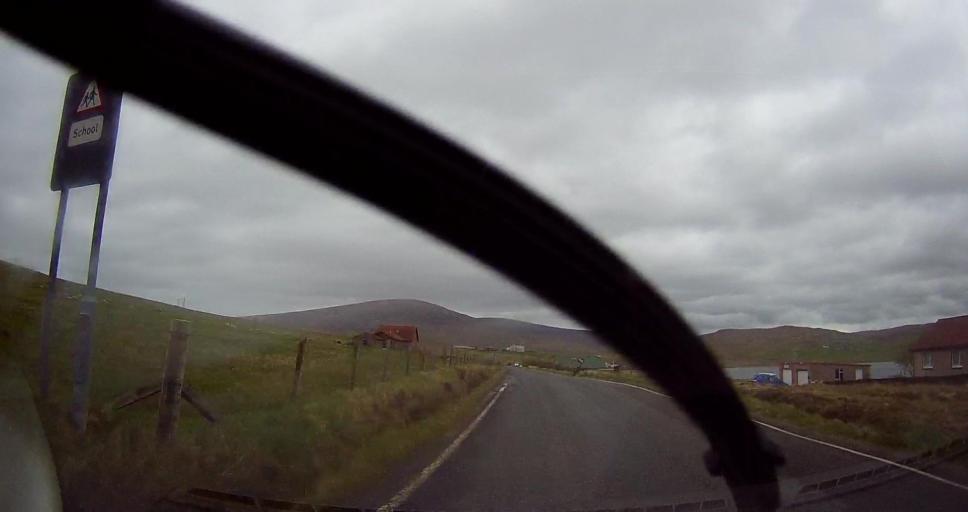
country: GB
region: Scotland
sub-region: Shetland Islands
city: Lerwick
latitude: 60.4856
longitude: -1.4688
